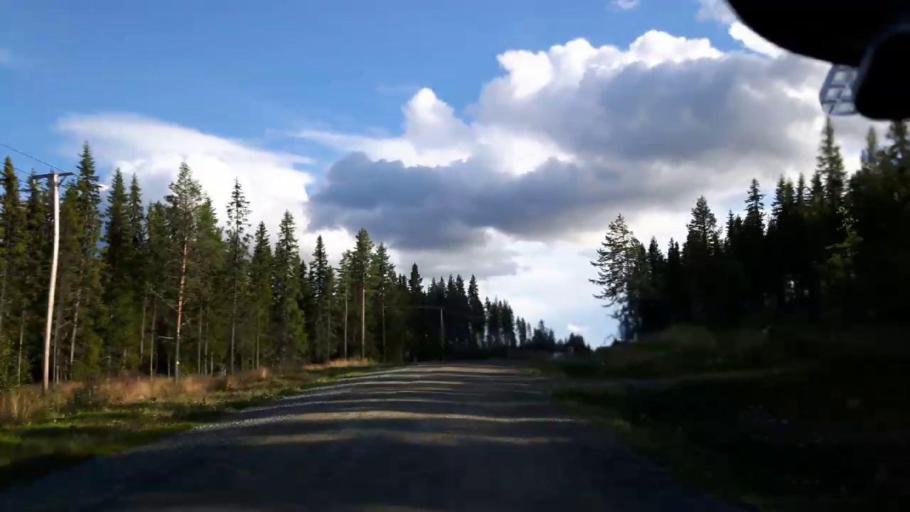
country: SE
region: Jaemtland
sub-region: Stroemsunds Kommun
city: Stroemsund
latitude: 63.3397
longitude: 15.5658
